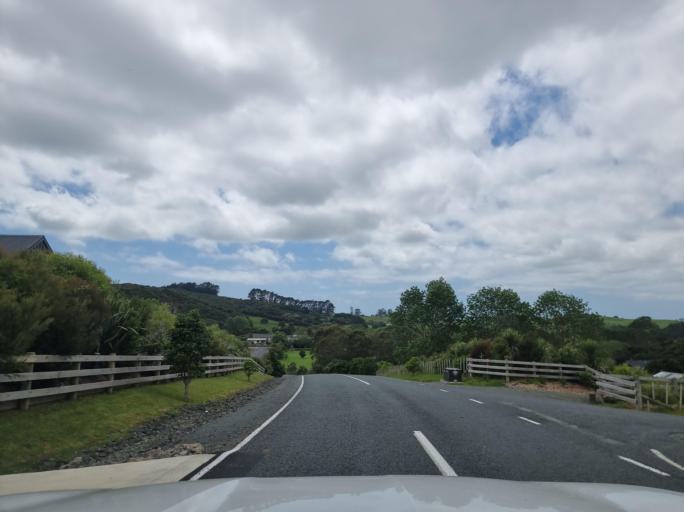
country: NZ
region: Northland
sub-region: Whangarei
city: Ruakaka
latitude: -36.0856
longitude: 174.5314
